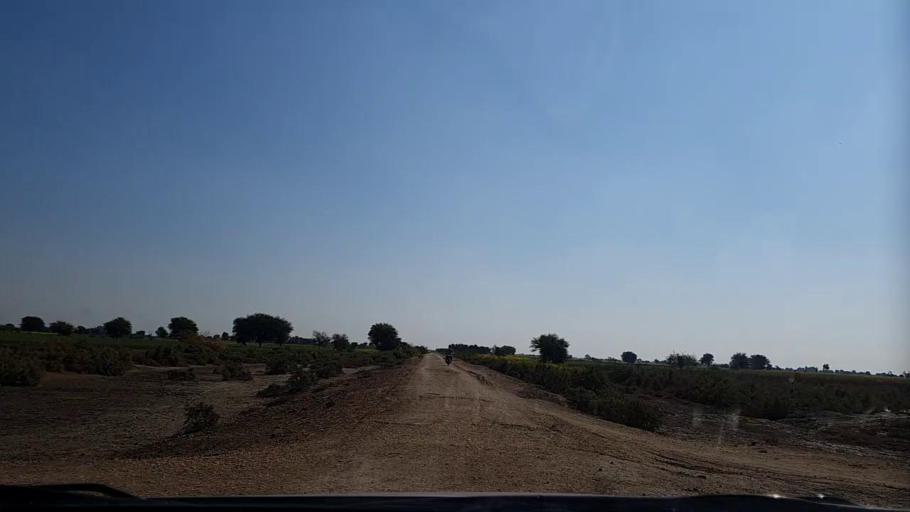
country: PK
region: Sindh
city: Pithoro
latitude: 25.7116
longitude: 69.3329
